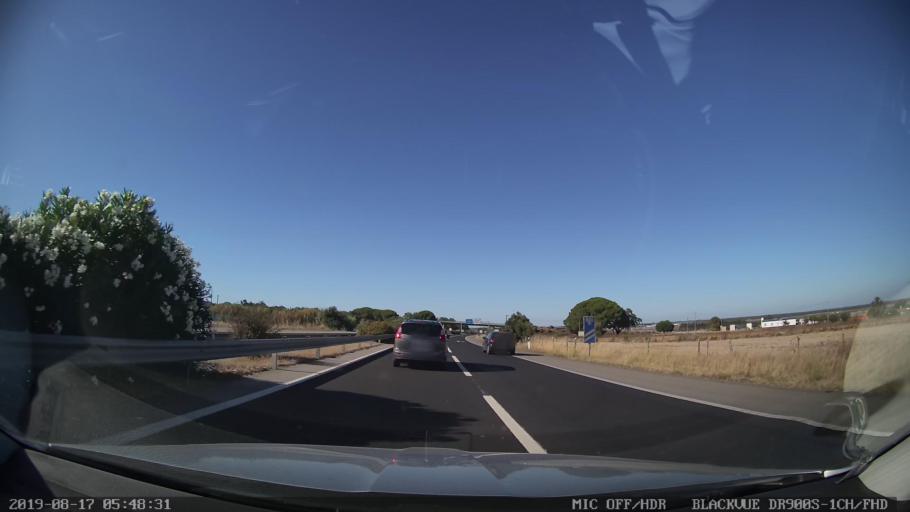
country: PT
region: Setubal
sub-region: Alcochete
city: Alcochete
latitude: 38.7360
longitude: -8.9344
